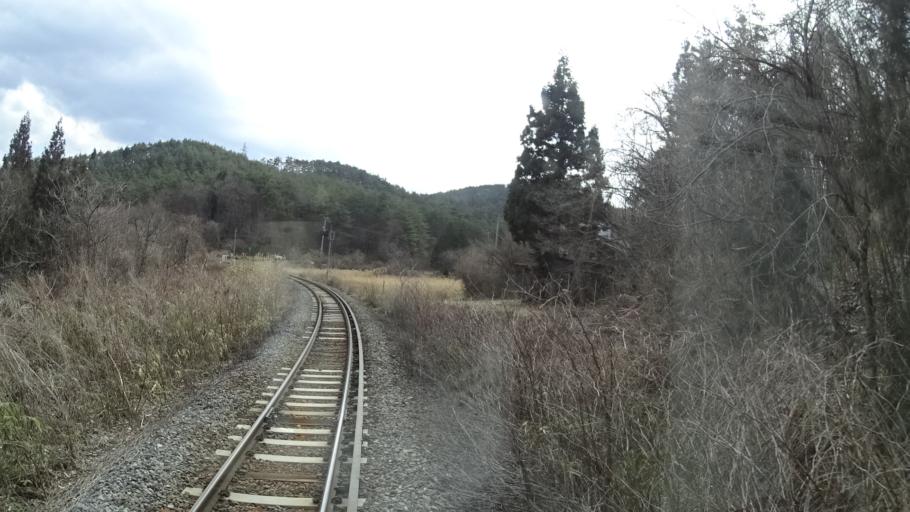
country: JP
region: Iwate
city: Tono
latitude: 39.3463
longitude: 141.3493
